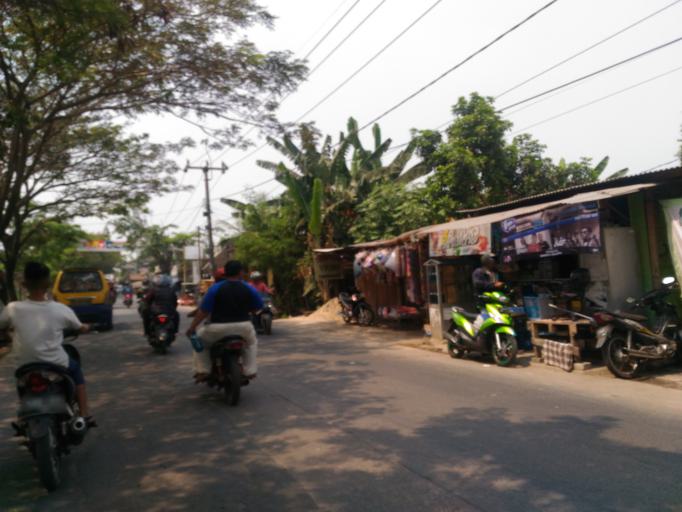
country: ID
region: West Java
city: Sepatan
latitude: -6.1473
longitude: 106.5725
